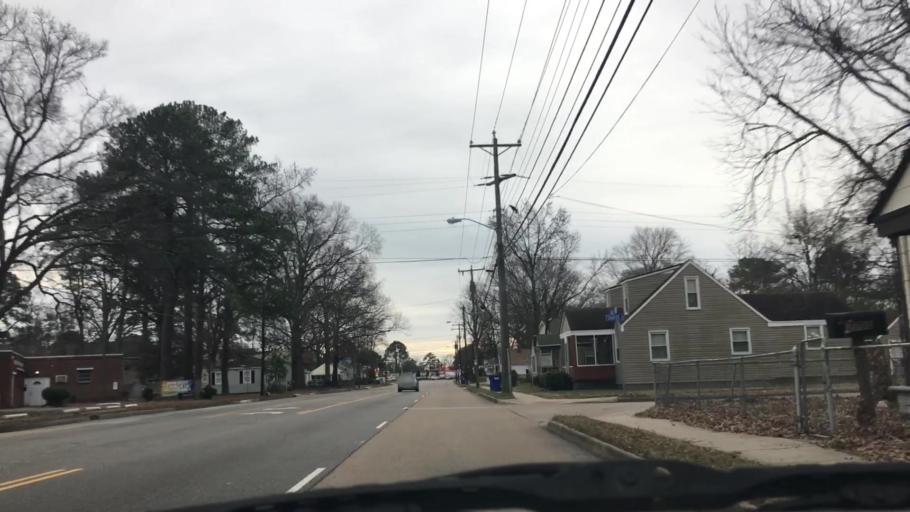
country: US
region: Virginia
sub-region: City of Norfolk
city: Norfolk
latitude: 36.8743
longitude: -76.2327
